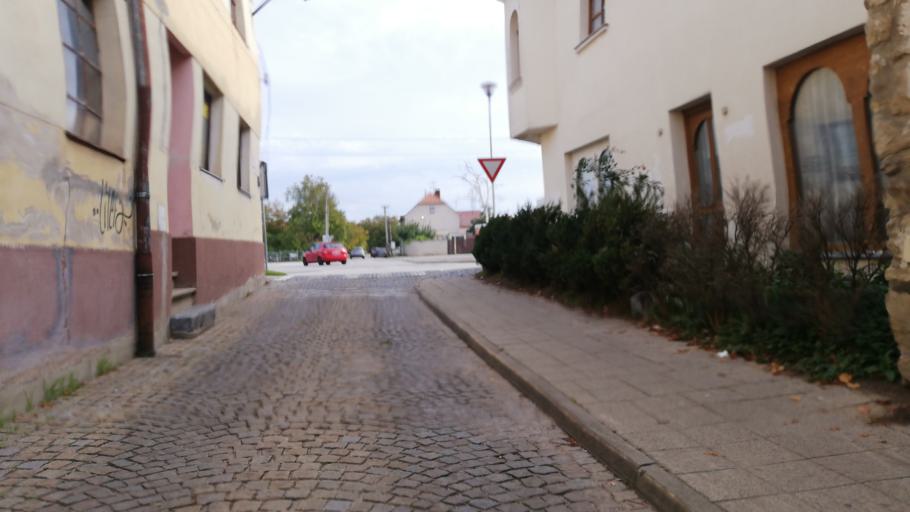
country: SK
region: Trnavsky
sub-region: Okres Skalica
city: Skalica
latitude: 48.8440
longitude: 17.2335
